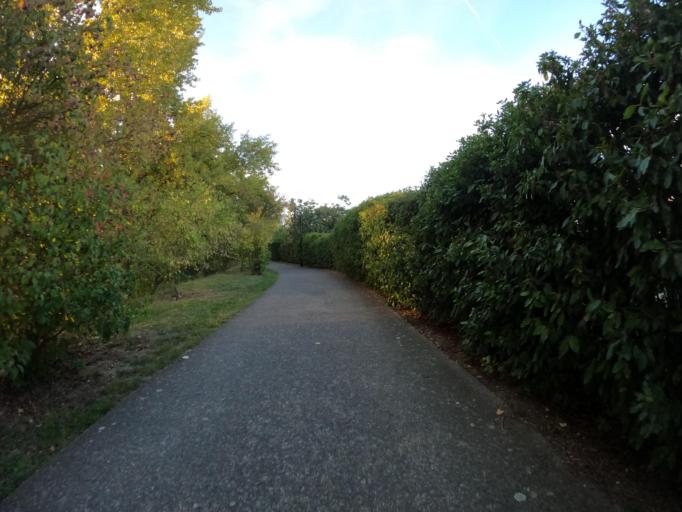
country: ES
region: Navarre
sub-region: Provincia de Navarra
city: Baranain
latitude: 42.8101
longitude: -1.6815
